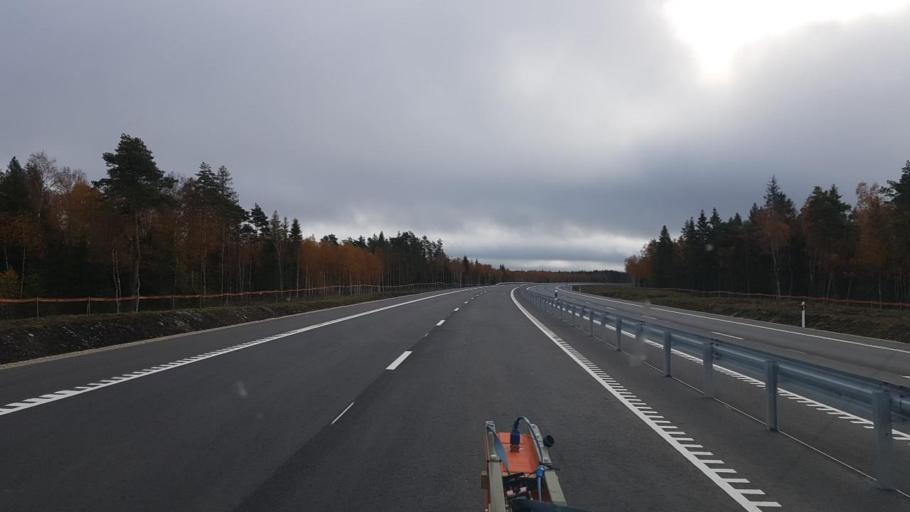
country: EE
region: Jaervamaa
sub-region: Paide linn
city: Paide
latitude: 59.0274
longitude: 25.5385
